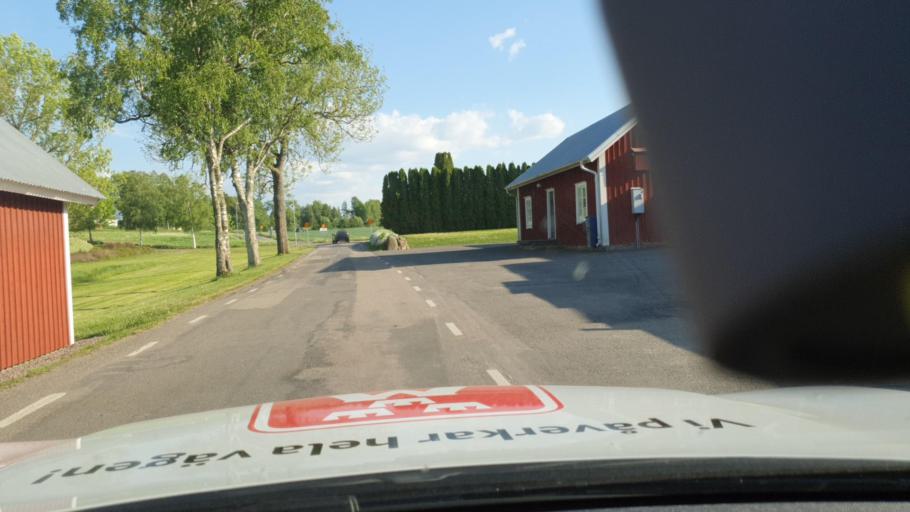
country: SE
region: Vaestra Goetaland
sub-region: Falkopings Kommun
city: Akarp
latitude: 58.1755
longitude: 13.6872
